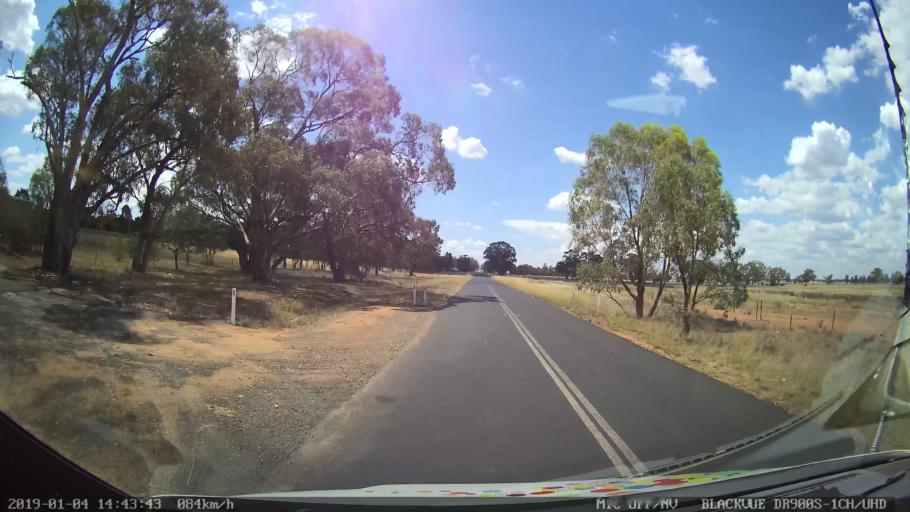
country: AU
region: New South Wales
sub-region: Dubbo Municipality
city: Dubbo
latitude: -32.1155
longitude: 148.6540
